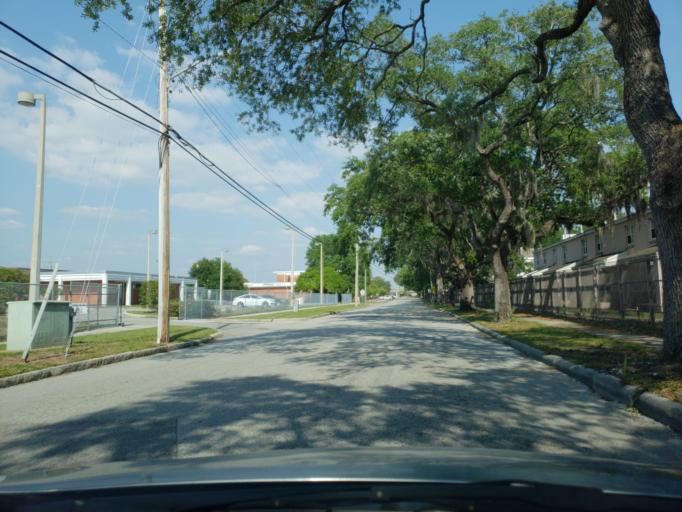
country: US
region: Florida
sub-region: Hillsborough County
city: Tampa
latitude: 27.9593
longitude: -82.4736
